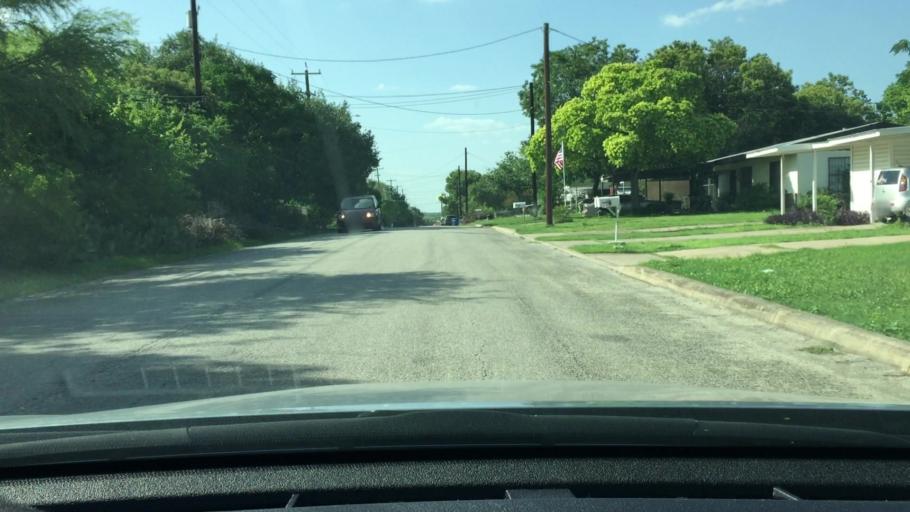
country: US
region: Texas
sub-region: Bexar County
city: Windcrest
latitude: 29.5312
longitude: -98.3837
